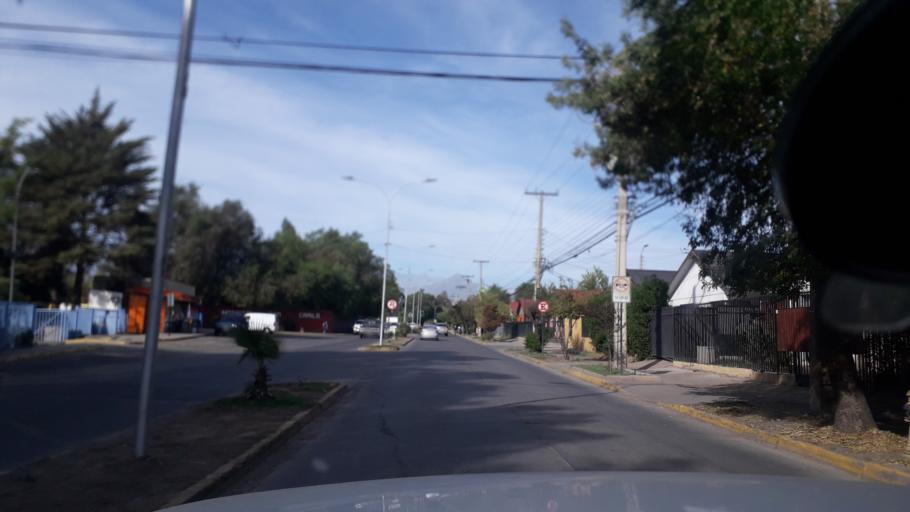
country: CL
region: Valparaiso
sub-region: Provincia de San Felipe
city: San Felipe
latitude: -32.7501
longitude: -70.7095
